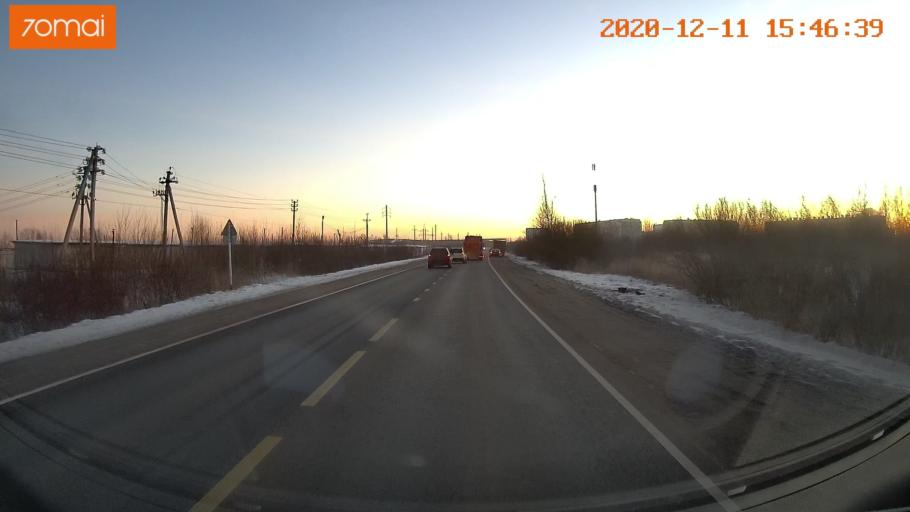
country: RU
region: Ivanovo
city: Novo-Talitsy
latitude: 57.0047
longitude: 40.8549
